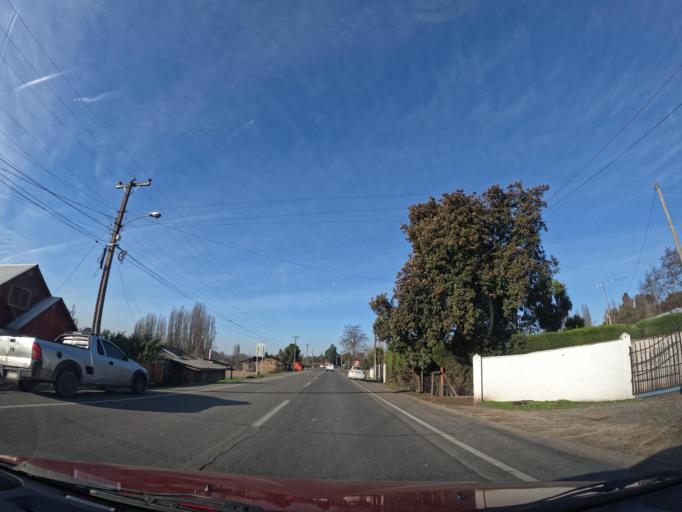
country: CL
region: Maule
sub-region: Provincia de Talca
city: San Clemente
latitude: -35.6225
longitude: -71.4932
